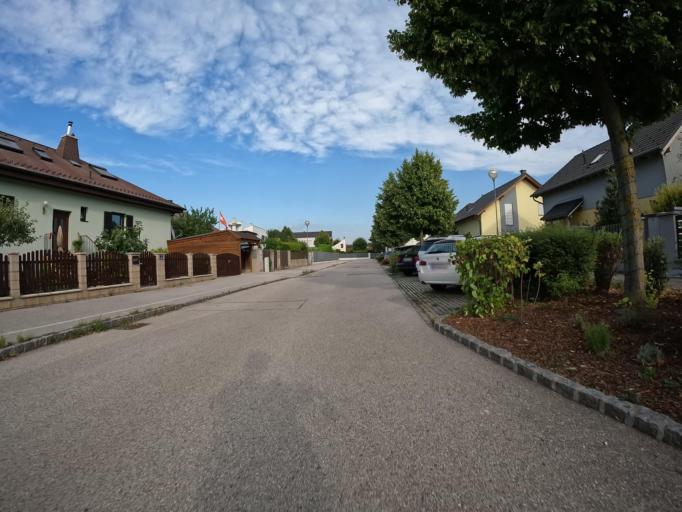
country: AT
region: Lower Austria
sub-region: Politischer Bezirk Baden
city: Traiskirchen
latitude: 48.0291
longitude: 16.3034
